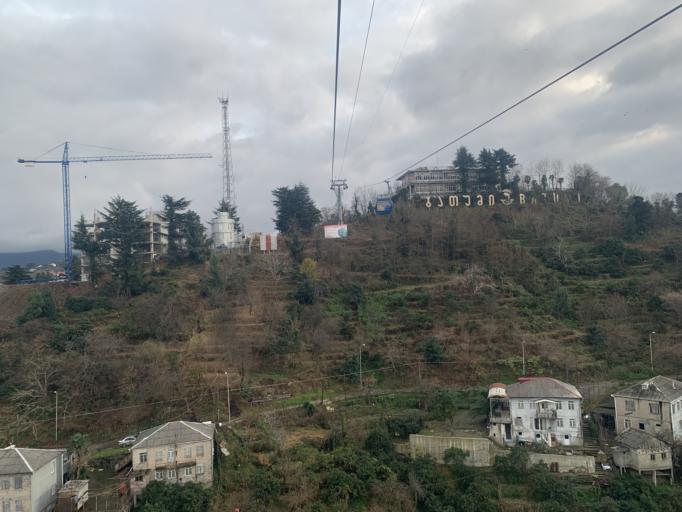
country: GE
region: Ajaria
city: Batumi
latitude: 41.6382
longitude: 41.6502
